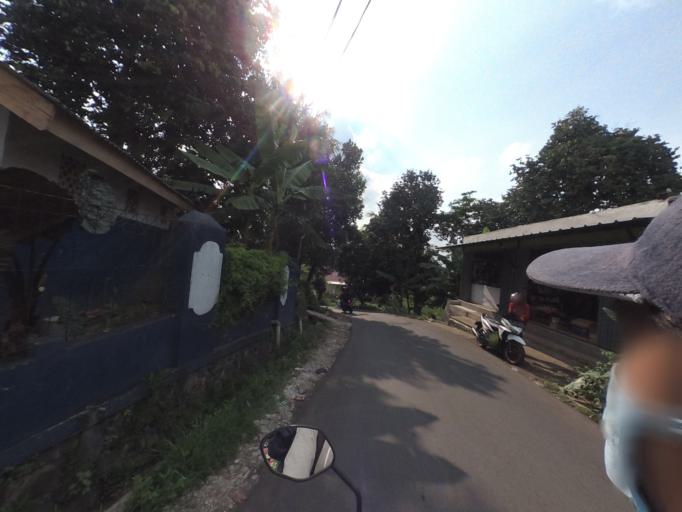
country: ID
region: West Java
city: Ciampea
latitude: -6.6059
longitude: 106.7081
